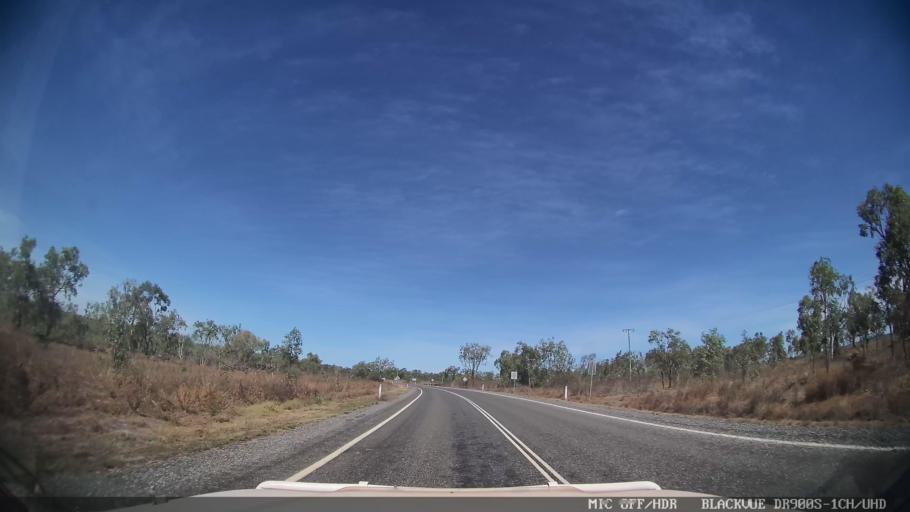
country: AU
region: Queensland
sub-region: Cook
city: Cooktown
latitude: -15.8636
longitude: 144.8036
